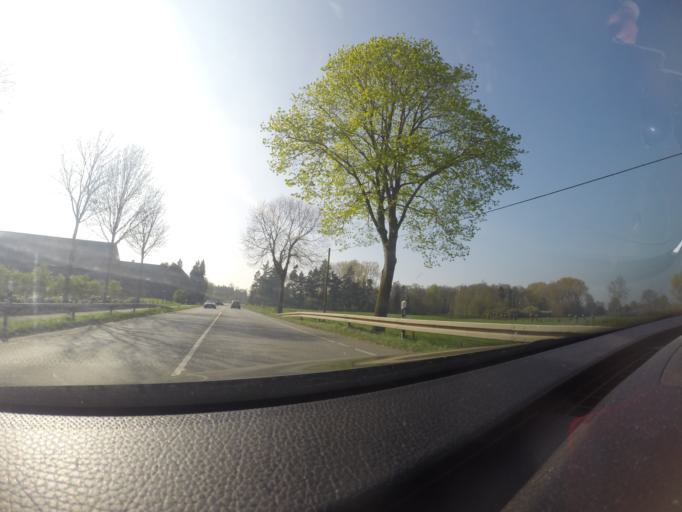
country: DE
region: North Rhine-Westphalia
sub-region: Regierungsbezirk Dusseldorf
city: Xanten
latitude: 51.6911
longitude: 6.3926
